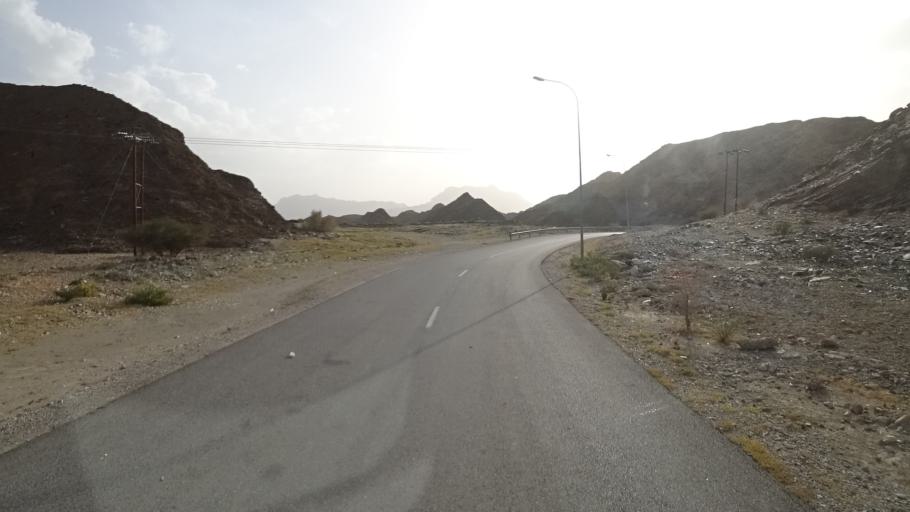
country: OM
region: Muhafazat Masqat
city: Bawshar
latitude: 23.3514
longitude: 58.5342
